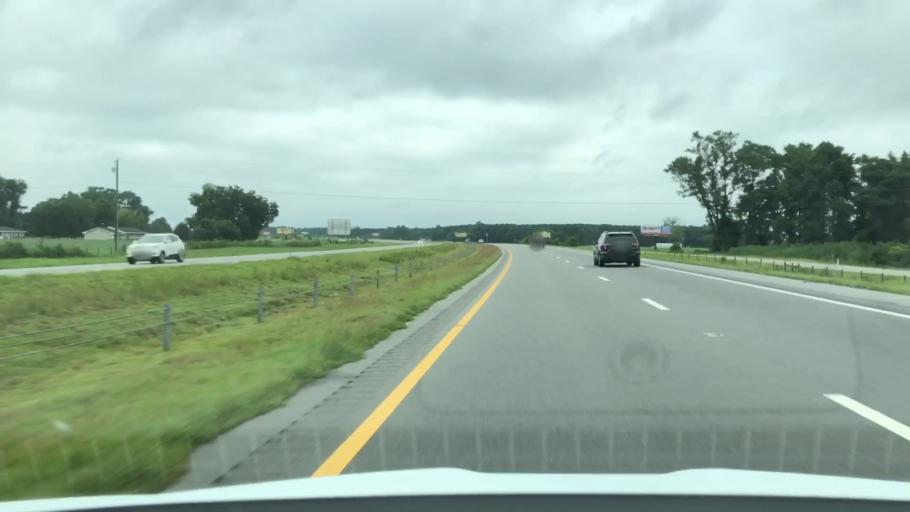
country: US
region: North Carolina
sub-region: Wayne County
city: Elroy
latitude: 35.3893
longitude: -77.8657
